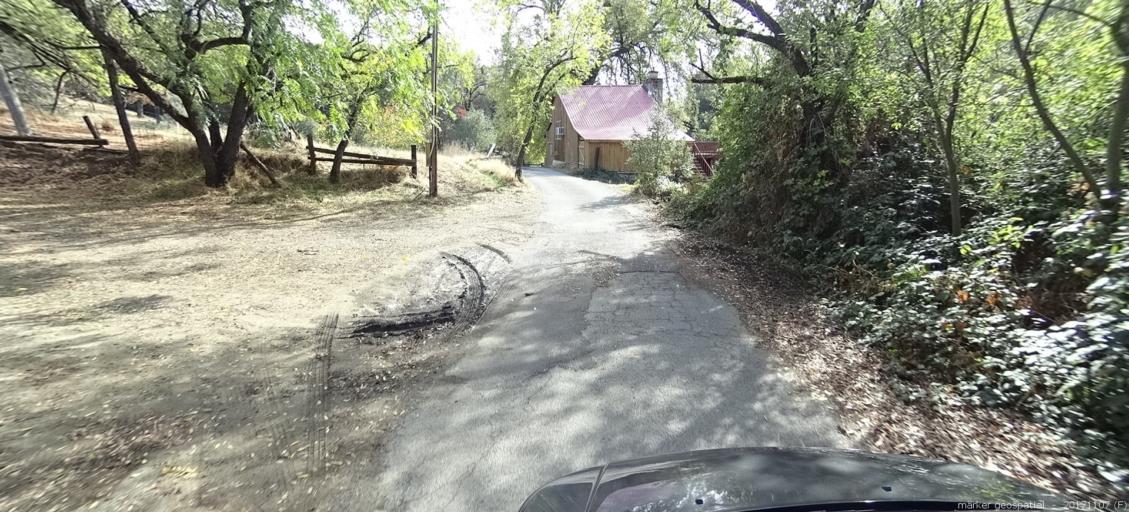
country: US
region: California
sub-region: Shasta County
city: Shasta
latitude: 40.5415
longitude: -122.5690
